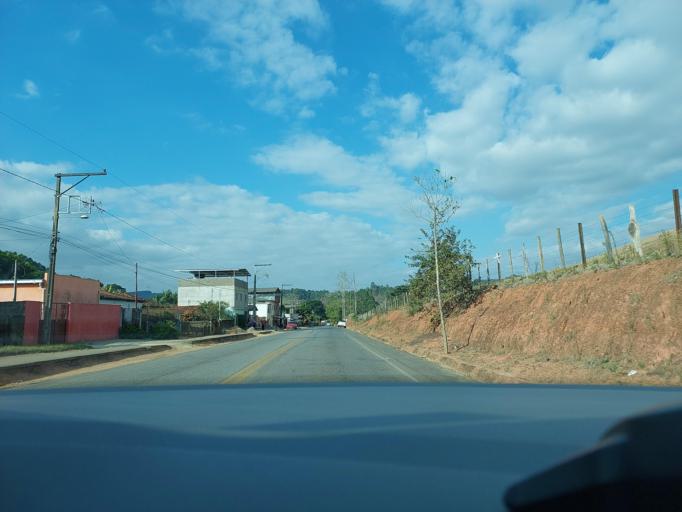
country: BR
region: Minas Gerais
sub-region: Vicosa
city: Vicosa
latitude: -20.8326
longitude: -42.7945
